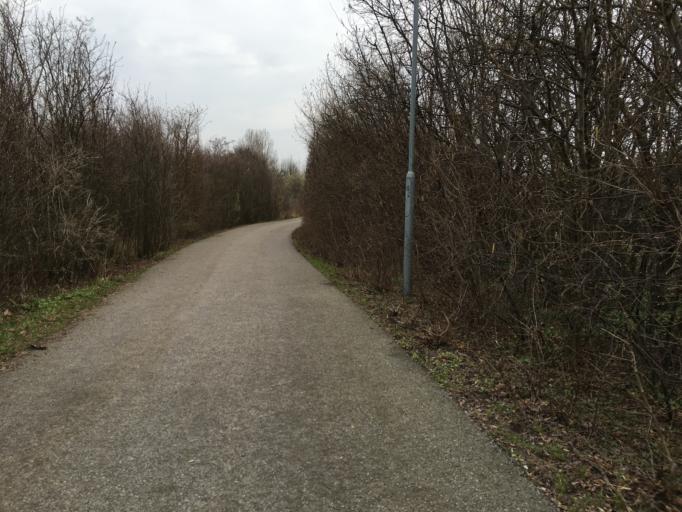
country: SE
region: Skane
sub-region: Lomma Kommun
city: Lomma
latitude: 55.6579
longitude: 13.0751
